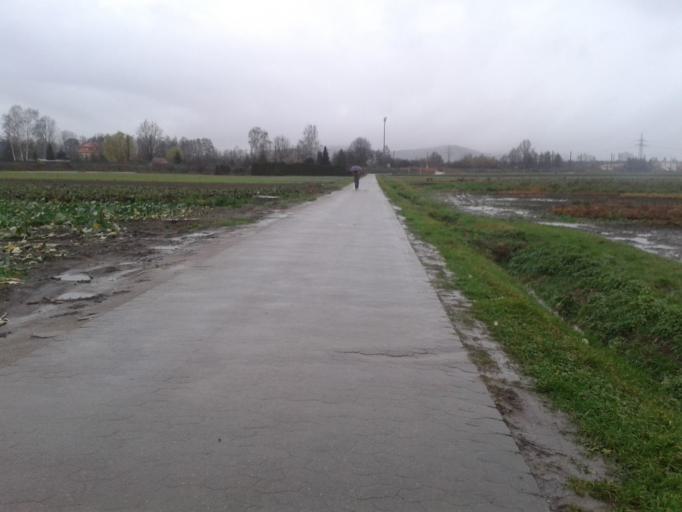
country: DE
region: Bavaria
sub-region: Upper Franconia
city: Bamberg
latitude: 49.9144
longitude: 10.8888
